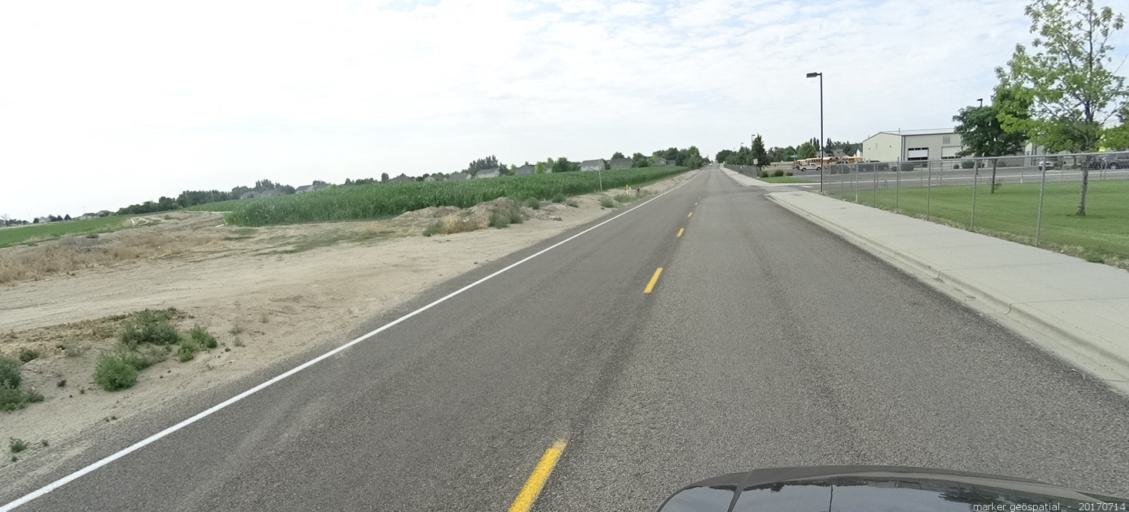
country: US
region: Idaho
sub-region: Ada County
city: Kuna
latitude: 43.4985
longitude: -116.4039
